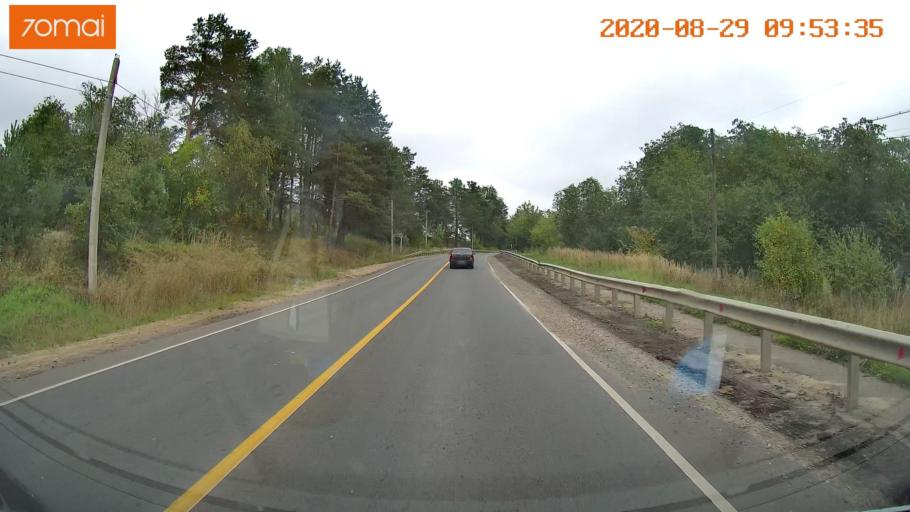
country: RU
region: Ivanovo
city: Zarechnyy
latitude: 57.4236
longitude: 42.2272
